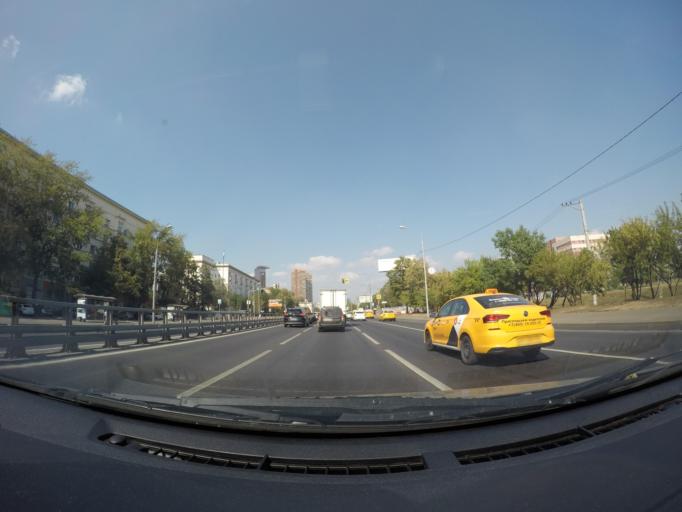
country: RU
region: Moscow
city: Novovladykino
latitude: 55.8125
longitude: 37.5784
